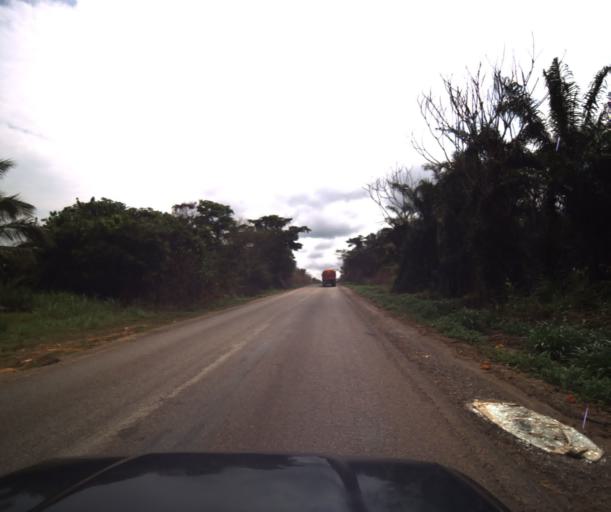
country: CM
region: Littoral
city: Edea
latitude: 3.8447
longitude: 10.4719
